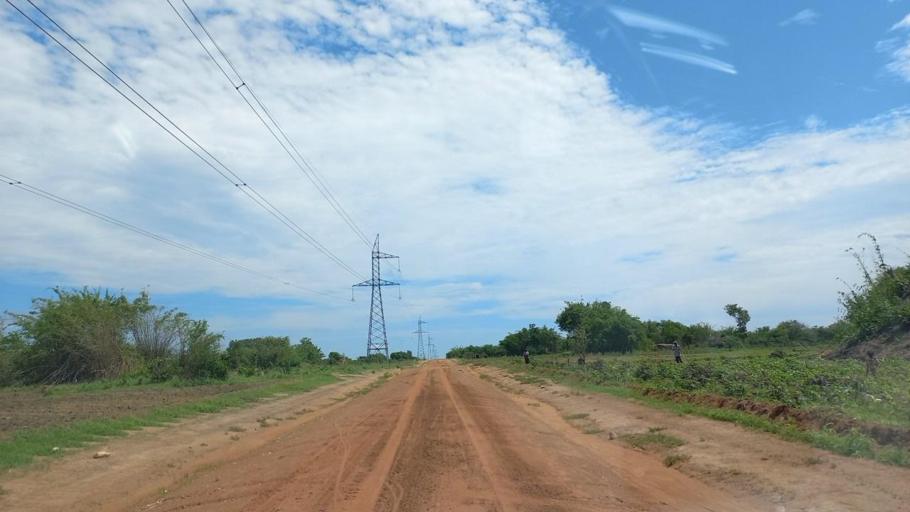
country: ZM
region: Copperbelt
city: Kitwe
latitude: -12.8451
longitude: 28.3369
